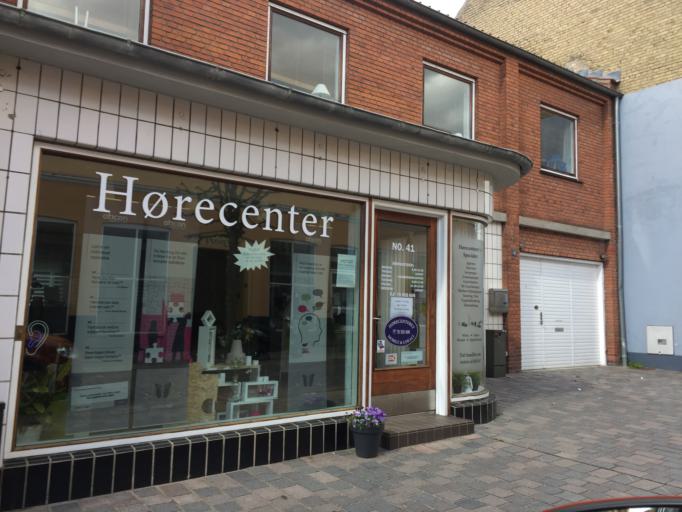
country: DK
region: Zealand
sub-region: Slagelse Kommune
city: Skaelskor
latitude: 55.2540
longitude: 11.2959
